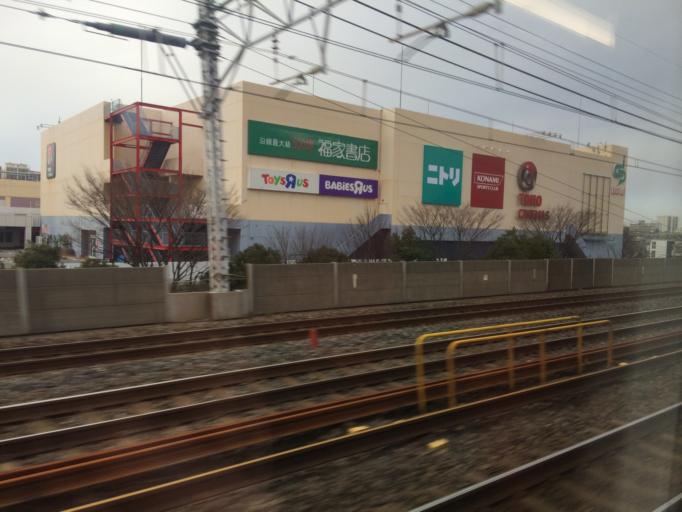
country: JP
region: Chiba
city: Funabashi
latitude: 35.7178
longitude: 139.9349
